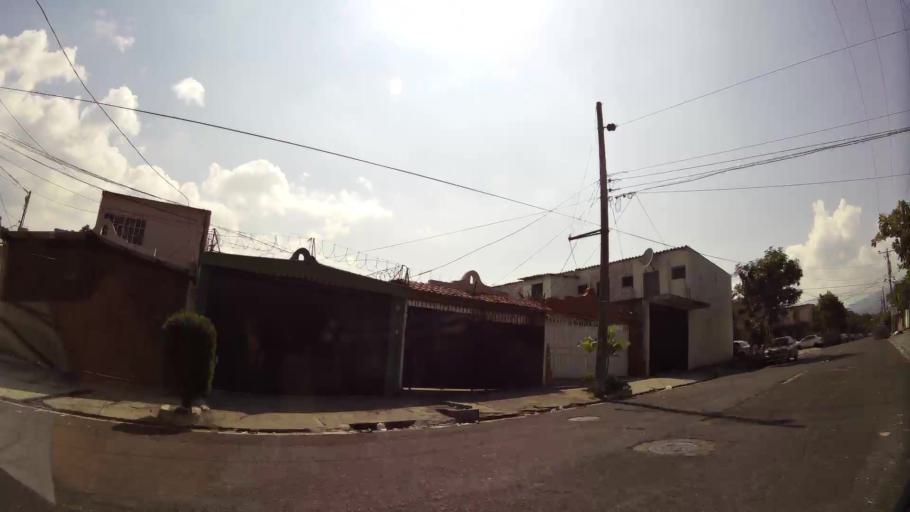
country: SV
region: San Salvador
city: Mejicanos
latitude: 13.7203
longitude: -89.2131
